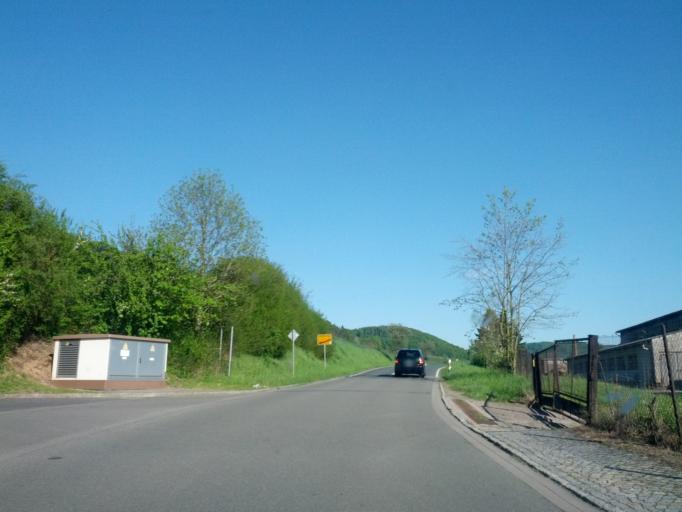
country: DE
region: Thuringia
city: Geismar
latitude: 51.2301
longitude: 10.1707
